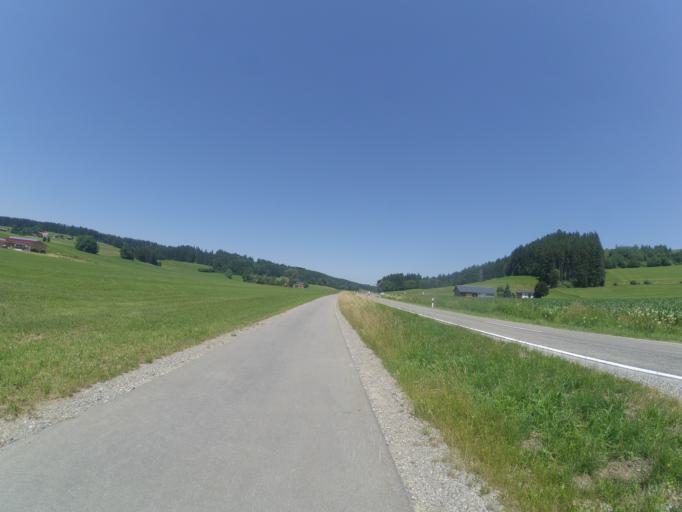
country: DE
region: Bavaria
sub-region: Swabia
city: Untrasried
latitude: 47.8426
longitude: 10.3539
